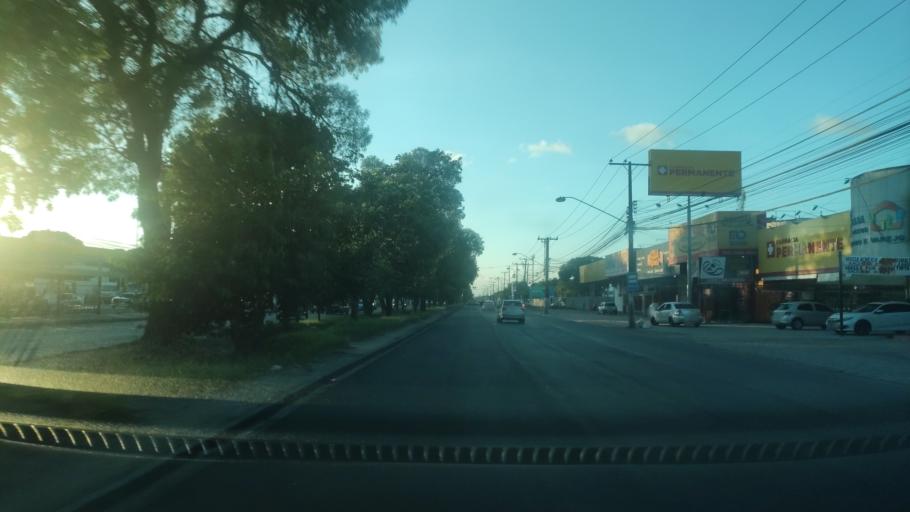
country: BR
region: Alagoas
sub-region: Satuba
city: Satuba
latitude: -9.5862
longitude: -35.7632
